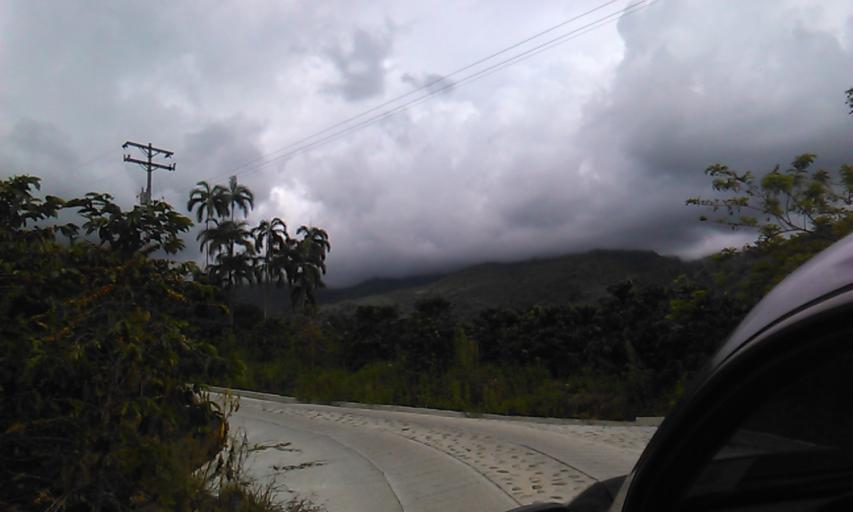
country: CO
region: Quindio
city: Cordoba
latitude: 4.4104
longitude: -75.6869
